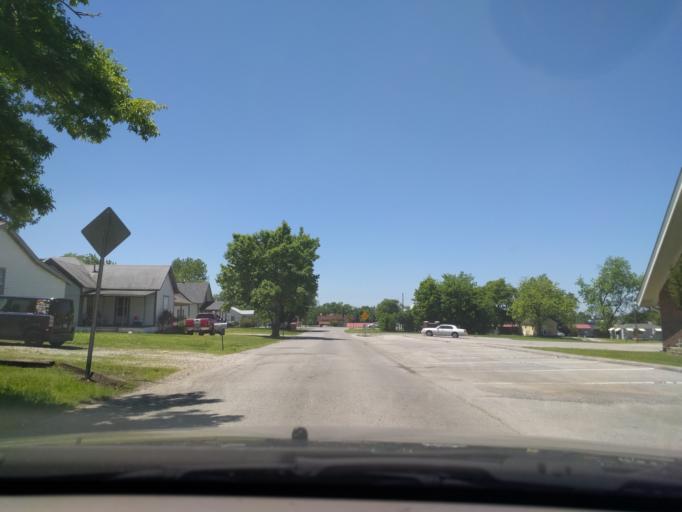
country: US
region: Oklahoma
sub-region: Tulsa County
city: Broken Arrow
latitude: 36.0535
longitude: -95.7958
